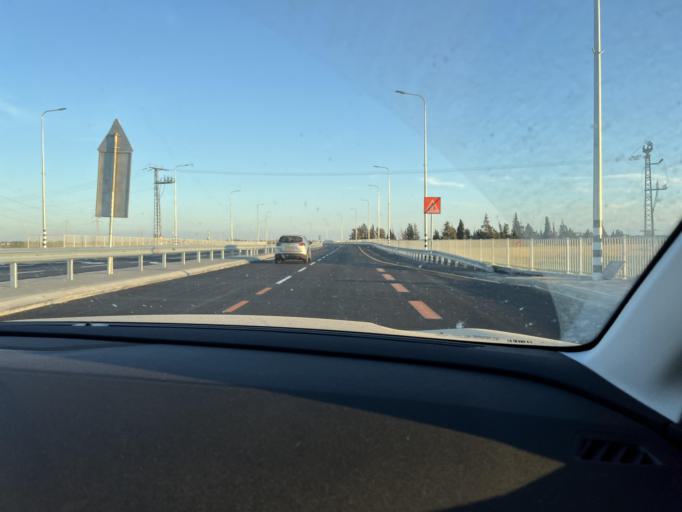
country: IL
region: Central District
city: Gan Yavne
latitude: 31.8176
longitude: 34.7034
